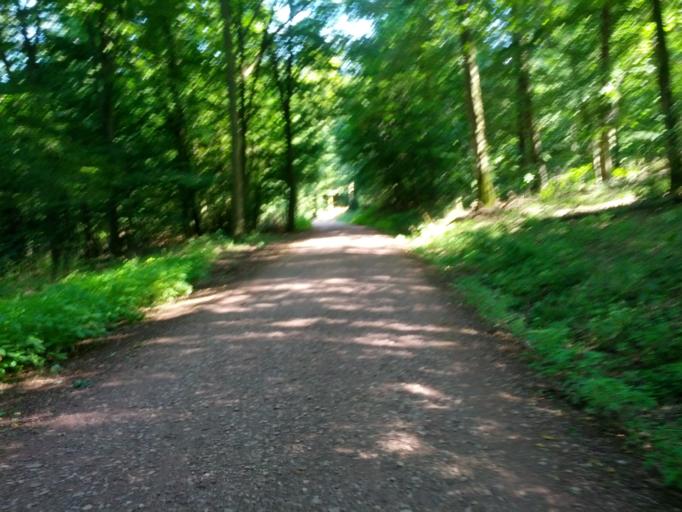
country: DE
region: Thuringia
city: Eisenach
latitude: 50.9518
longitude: 10.3069
